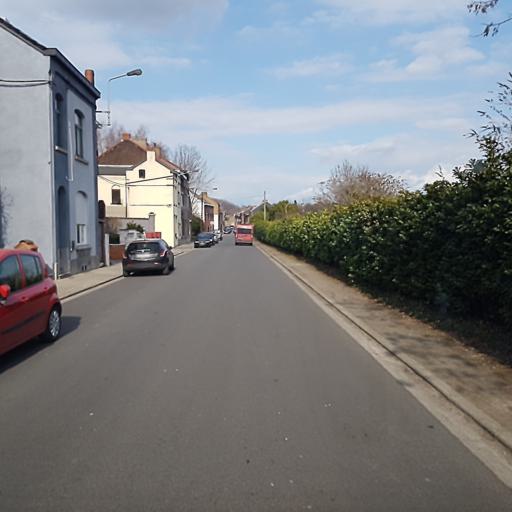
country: BE
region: Wallonia
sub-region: Province du Hainaut
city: Charleroi
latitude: 50.4263
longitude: 4.4448
